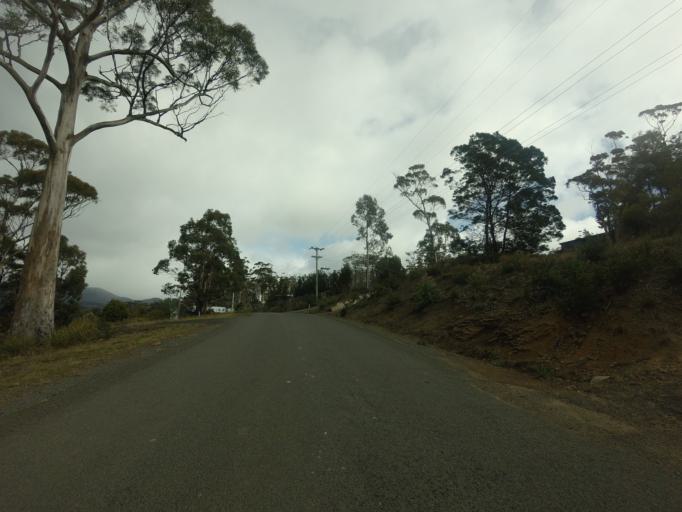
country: AU
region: Tasmania
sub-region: Sorell
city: Sorell
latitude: -42.5394
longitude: 147.9120
